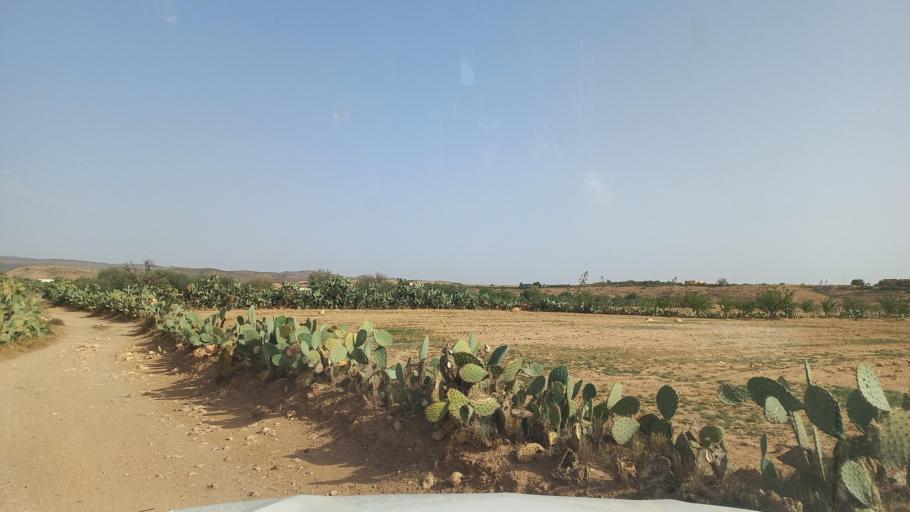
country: TN
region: Al Qasrayn
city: Kasserine
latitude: 35.2980
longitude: 8.9632
